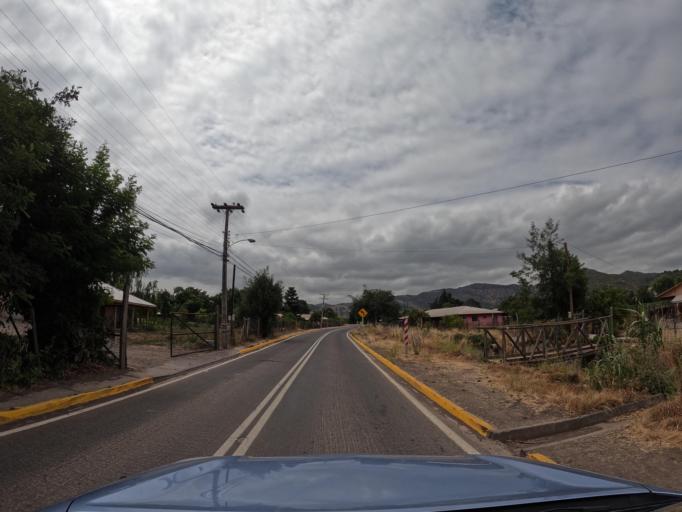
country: CL
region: Maule
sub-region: Provincia de Curico
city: Teno
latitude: -34.7744
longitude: -71.1842
